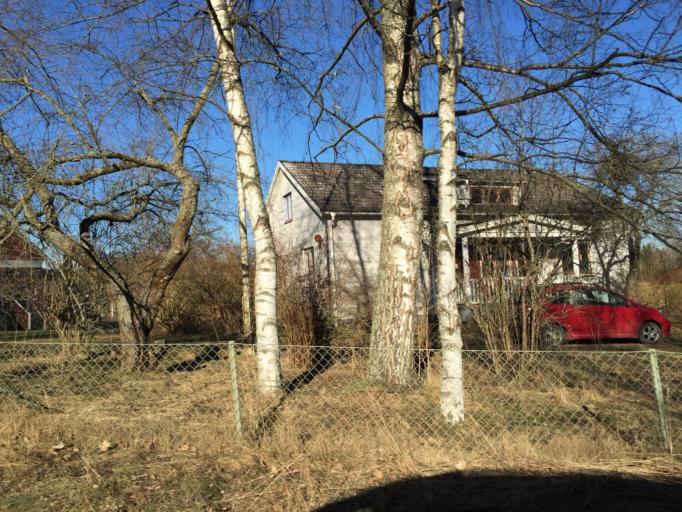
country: SE
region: OEstergoetland
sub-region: Finspangs Kommun
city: Finspang
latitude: 58.7203
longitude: 15.6420
